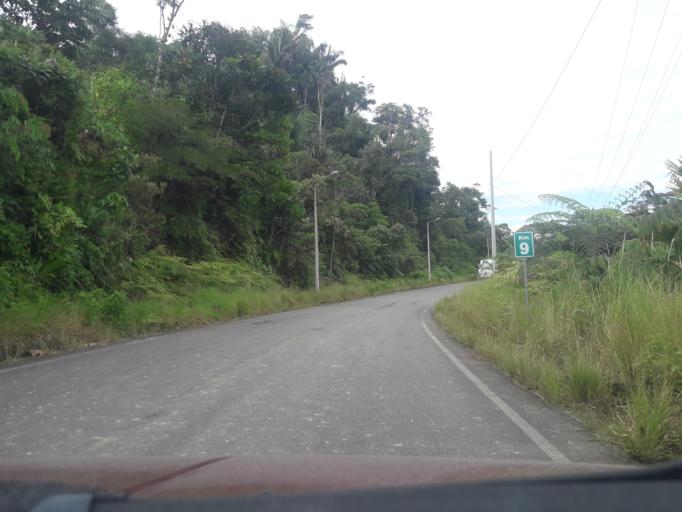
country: EC
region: Napo
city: Tena
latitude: -1.0271
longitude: -77.8869
